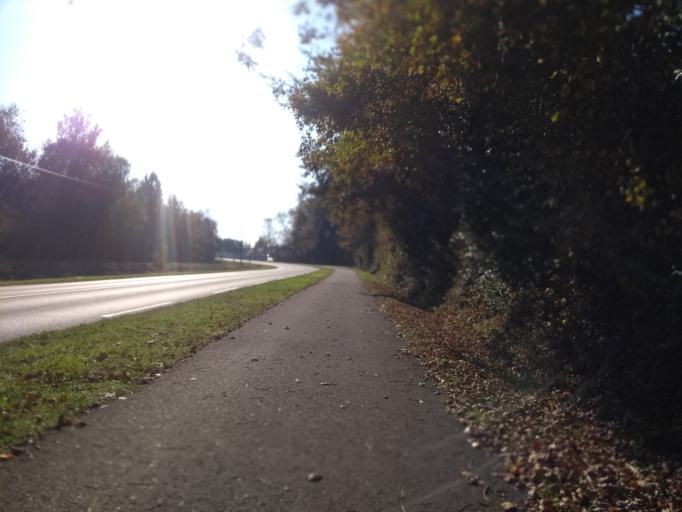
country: FR
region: Aquitaine
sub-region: Departement de la Gironde
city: Leognan
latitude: 44.7468
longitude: -0.6178
